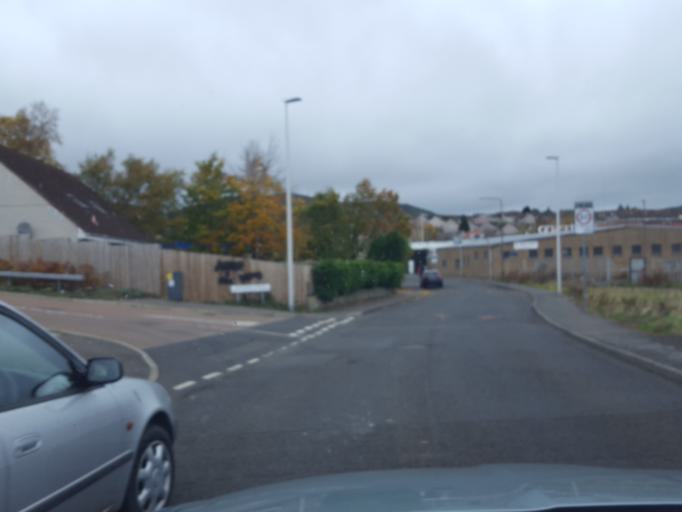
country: GB
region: Scotland
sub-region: Midlothian
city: Penicuik
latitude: 55.8340
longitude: -3.2195
